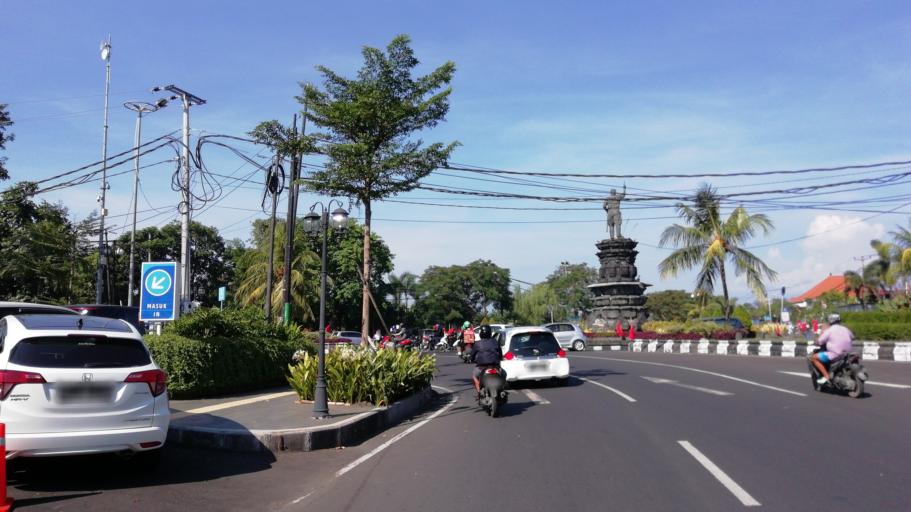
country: ID
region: Bali
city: Banjar Batanpoh
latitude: -8.6734
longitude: 115.2444
